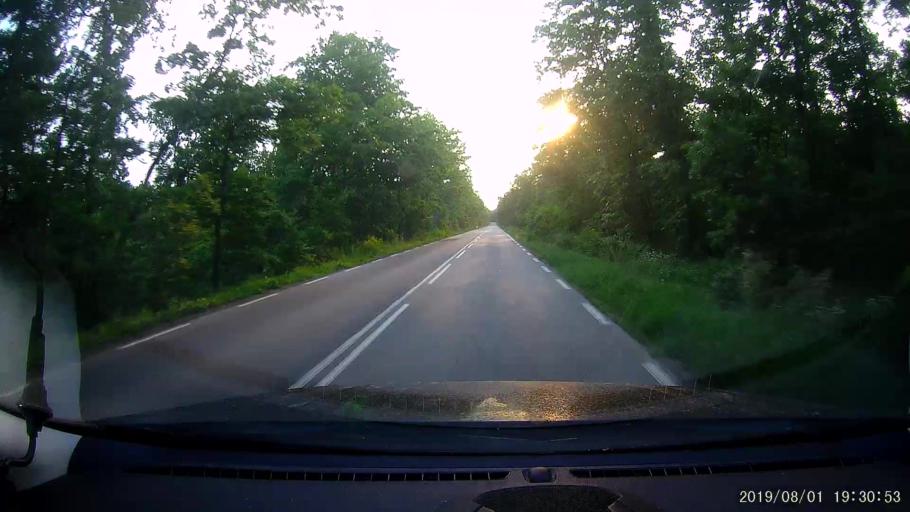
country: BG
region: Burgas
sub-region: Obshtina Sungurlare
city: Sungurlare
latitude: 42.8098
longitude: 26.8854
